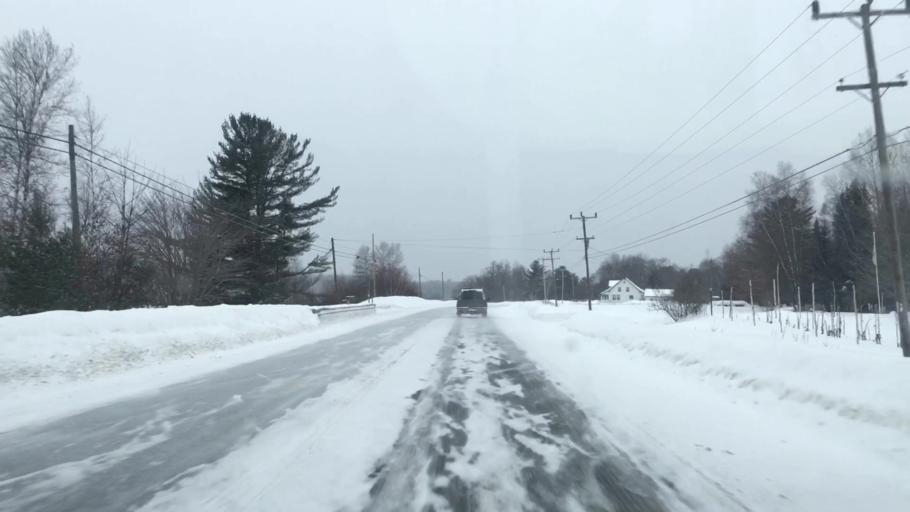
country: US
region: Maine
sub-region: Penobscot County
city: Medway
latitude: 45.5952
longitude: -68.4883
